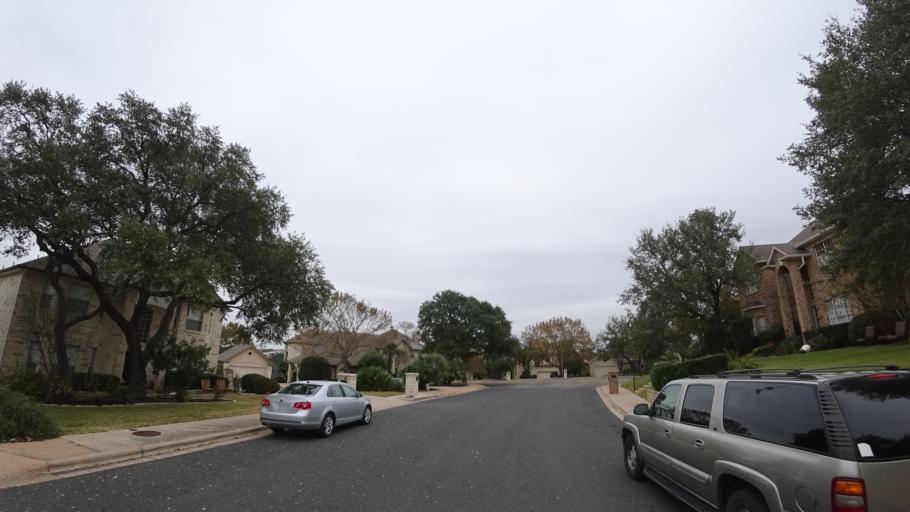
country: US
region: Texas
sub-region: Travis County
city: West Lake Hills
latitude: 30.3707
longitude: -97.7937
